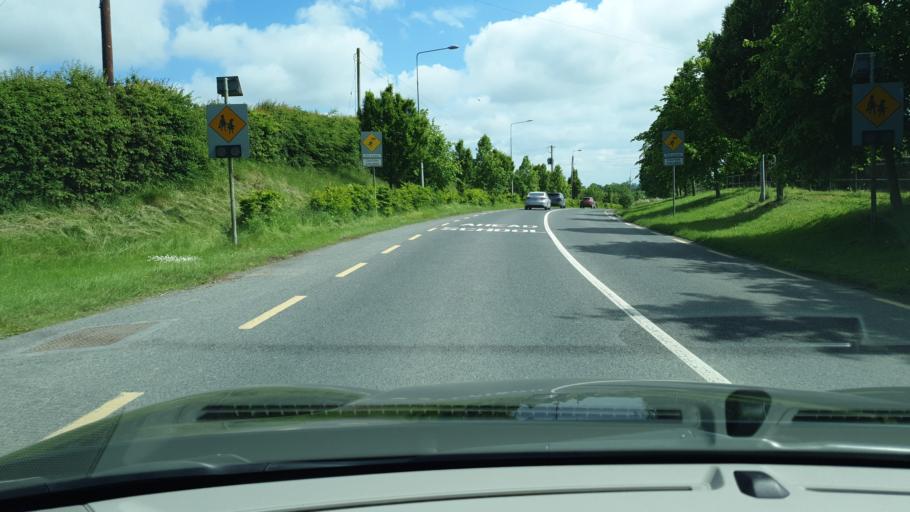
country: IE
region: Ulster
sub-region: An Cabhan
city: Kingscourt
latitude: 53.8190
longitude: -6.7421
